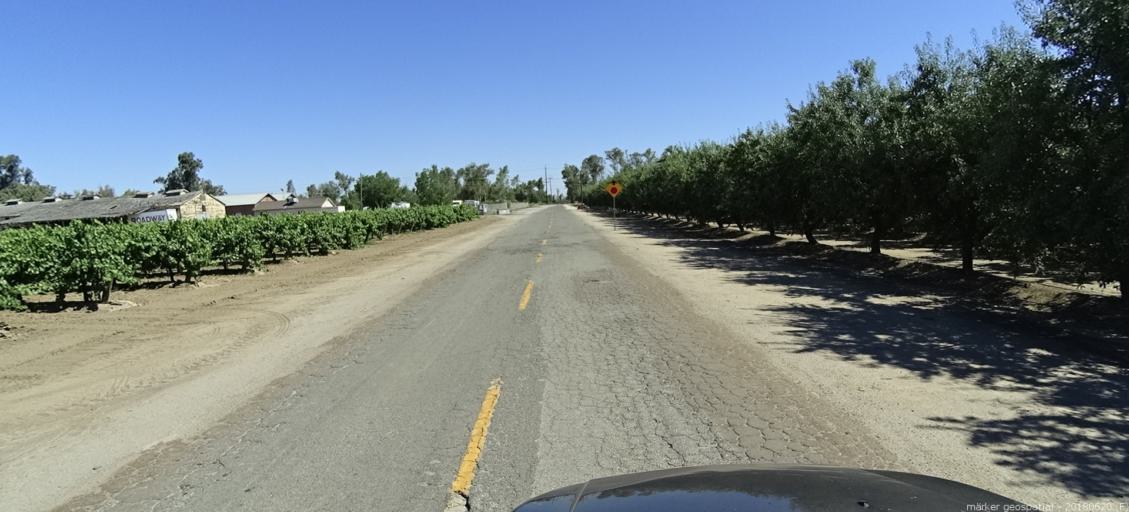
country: US
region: California
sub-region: Madera County
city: Parkwood
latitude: 36.9073
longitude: -120.0285
